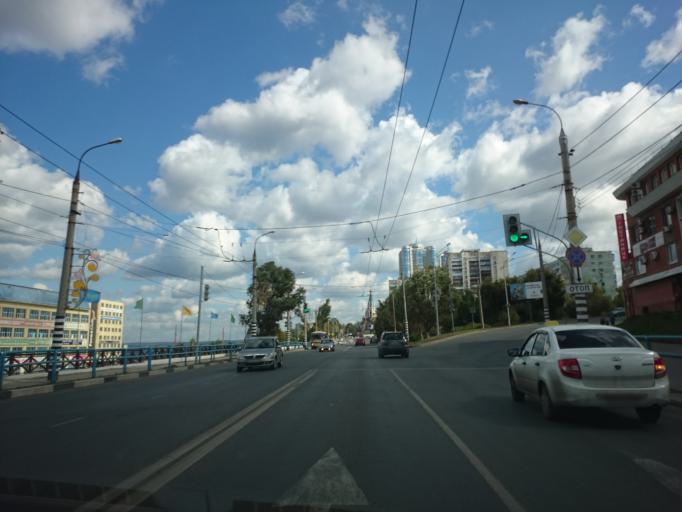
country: RU
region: Samara
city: Samara
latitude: 53.2124
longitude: 50.1268
